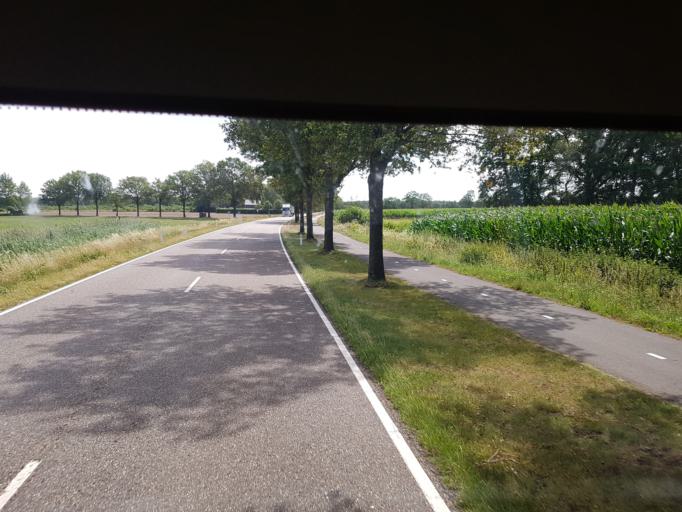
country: NL
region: Limburg
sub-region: Gemeente Nederweert
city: Nederweert
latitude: 51.2646
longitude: 5.7840
